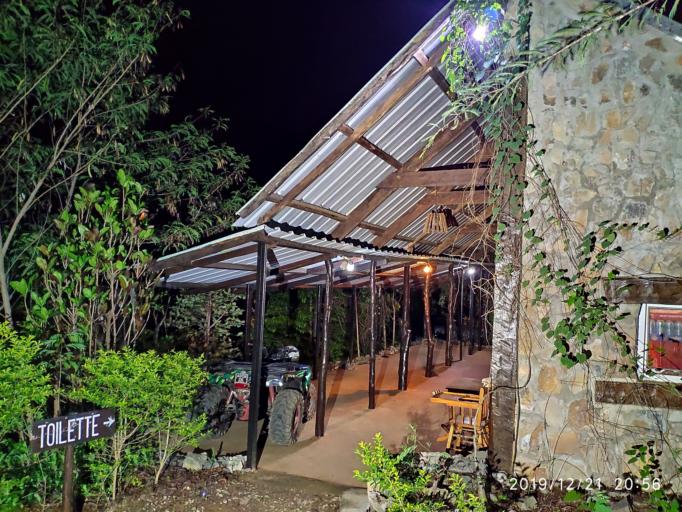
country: MG
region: Diana
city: Ambilobe
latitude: -12.9619
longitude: 49.1488
